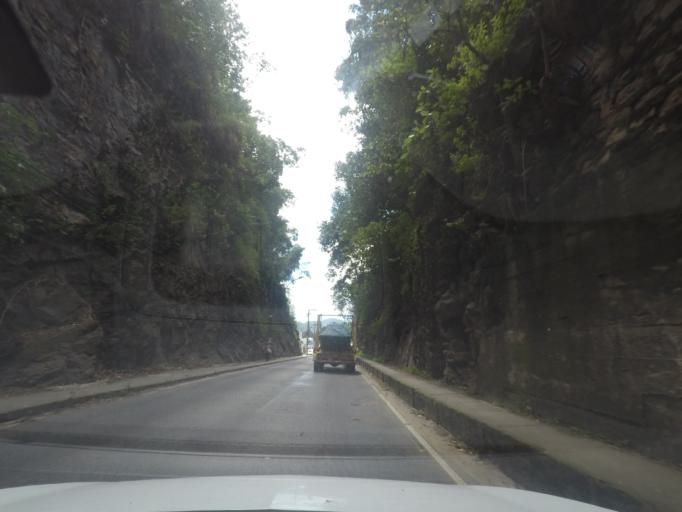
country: BR
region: Rio de Janeiro
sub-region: Teresopolis
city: Teresopolis
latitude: -22.4020
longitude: -42.9714
